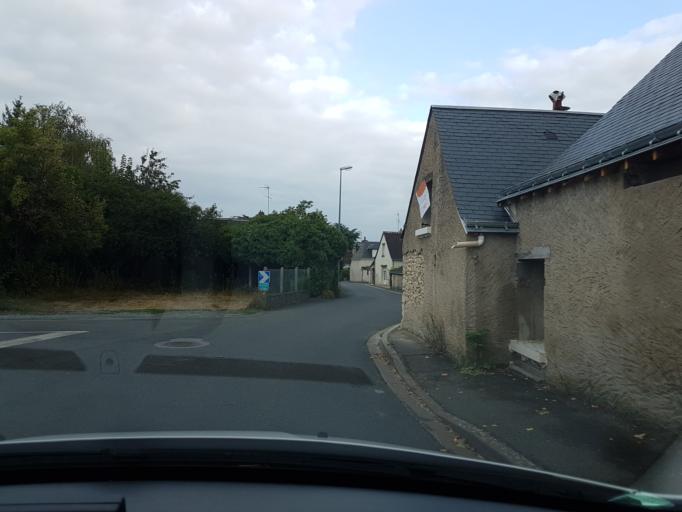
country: FR
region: Centre
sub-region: Departement d'Indre-et-Loire
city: Saint-Avertin
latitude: 47.3658
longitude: 0.7548
